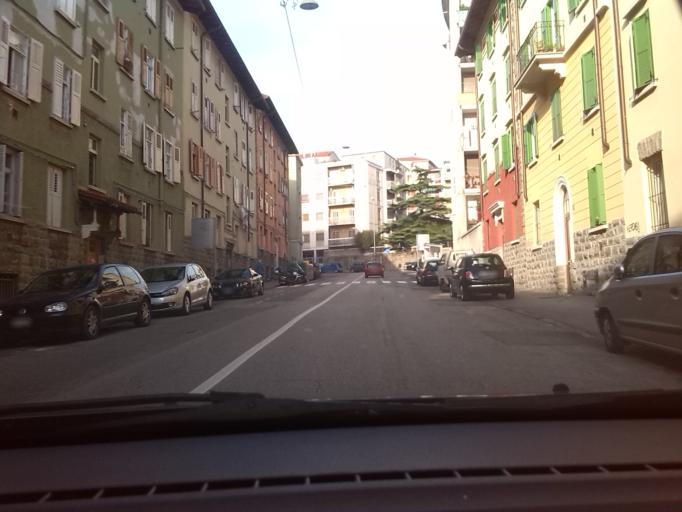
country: IT
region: Friuli Venezia Giulia
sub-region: Provincia di Trieste
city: Trieste
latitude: 45.6381
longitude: 13.7812
